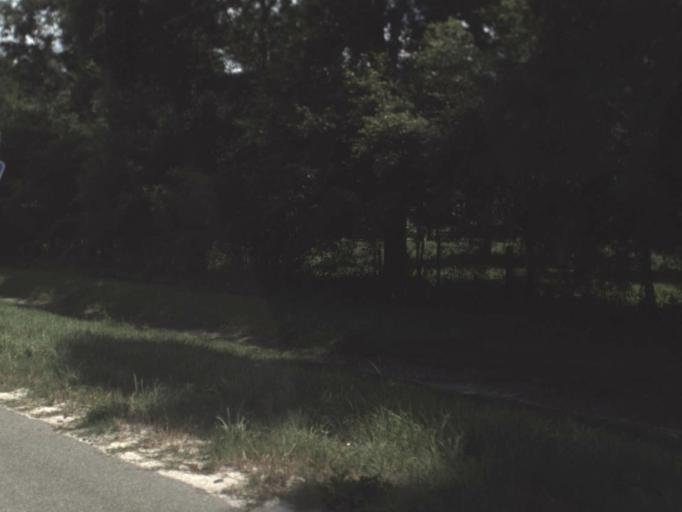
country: US
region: Florida
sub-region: Lafayette County
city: Mayo
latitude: 29.9826
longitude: -82.9971
